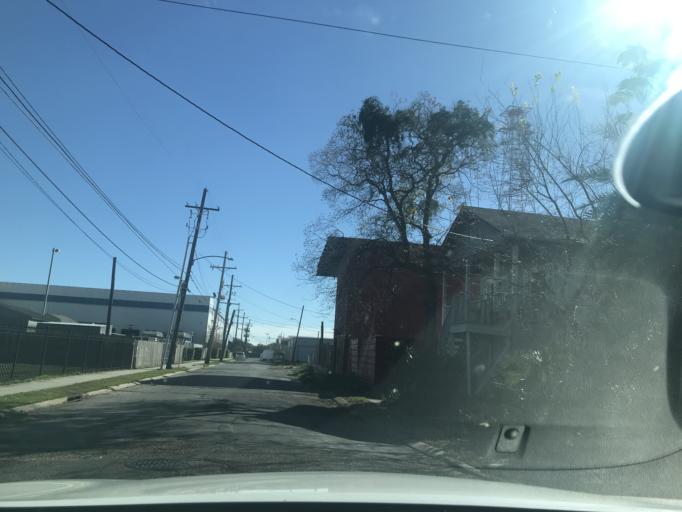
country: US
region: Louisiana
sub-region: Orleans Parish
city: New Orleans
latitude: 29.9556
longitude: -90.0994
